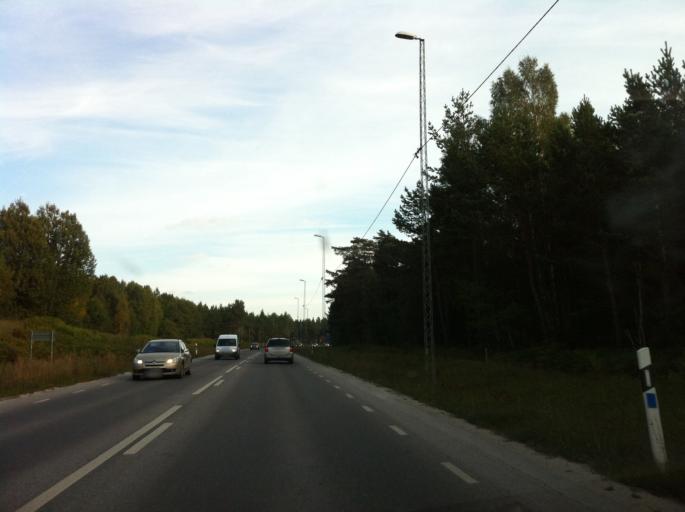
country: SE
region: Gotland
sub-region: Gotland
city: Visby
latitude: 57.6105
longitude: 18.2943
